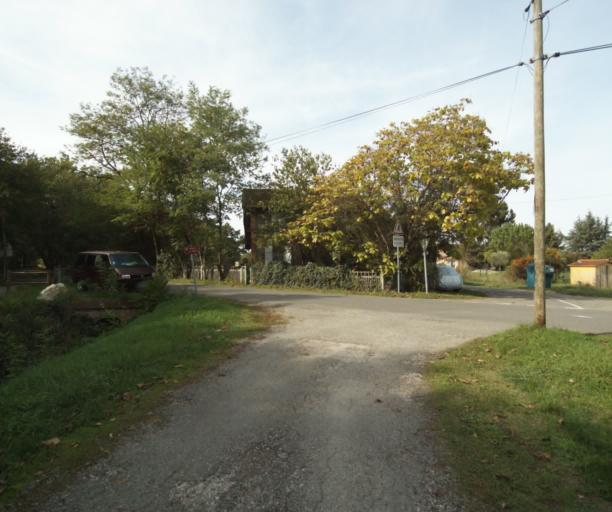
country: FR
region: Midi-Pyrenees
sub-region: Departement du Tarn-et-Garonne
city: Orgueil
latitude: 43.9085
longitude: 1.3915
